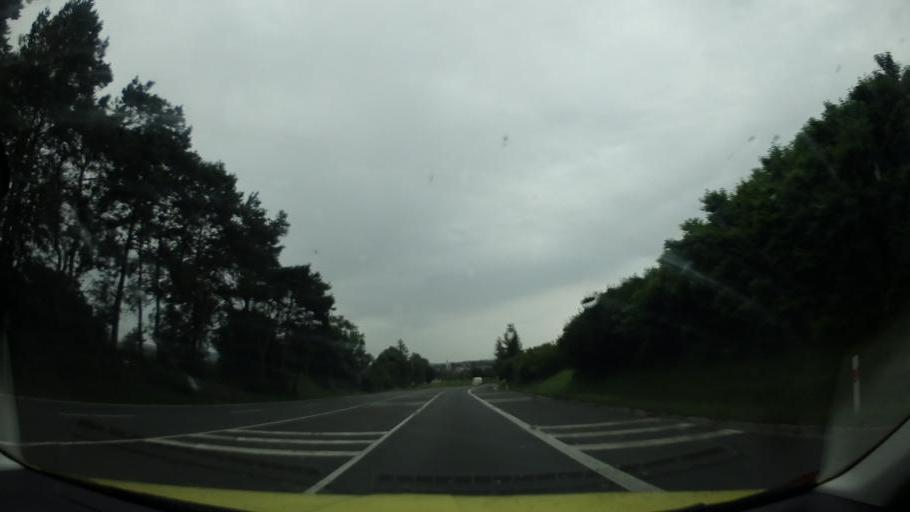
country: CZ
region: Olomoucky
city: Belotin
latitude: 49.5783
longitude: 17.7827
